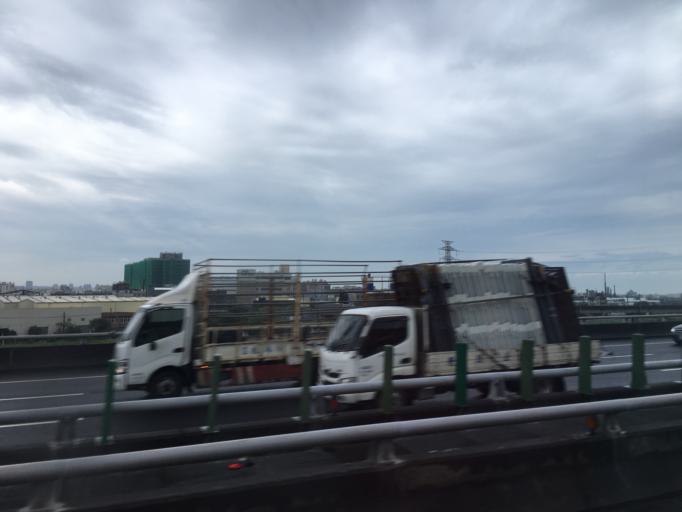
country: TW
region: Taiwan
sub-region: Hsinchu
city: Zhubei
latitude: 24.8509
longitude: 121.0165
